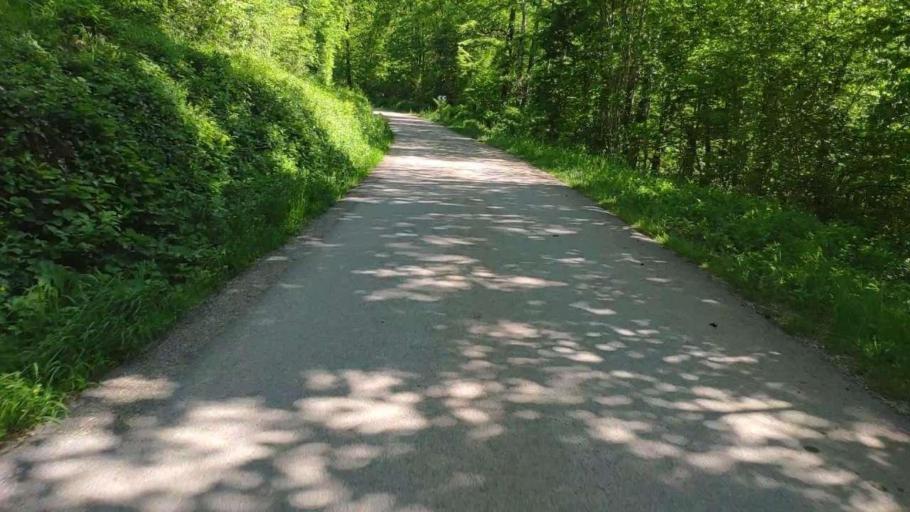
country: FR
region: Franche-Comte
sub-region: Departement du Jura
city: Poligny
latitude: 46.7441
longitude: 5.7738
